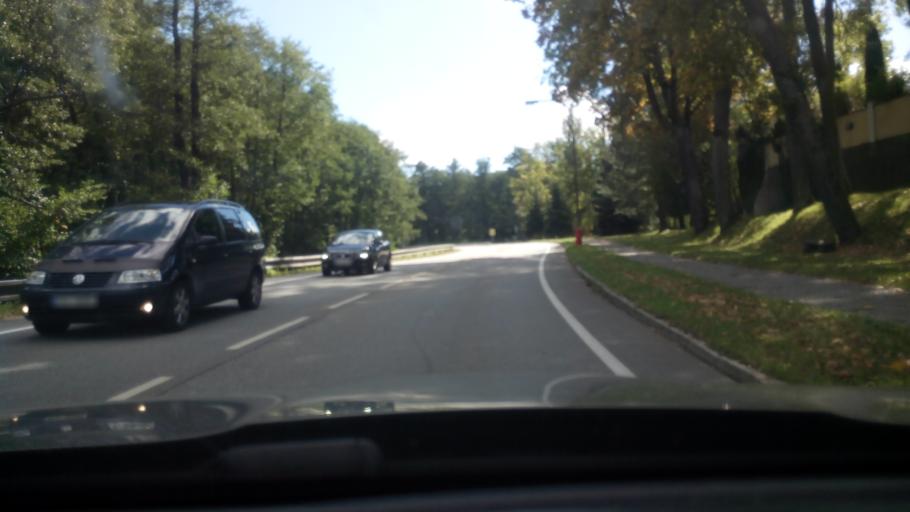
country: CZ
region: Jihocesky
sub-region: Okres Prachatice
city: Zdikov
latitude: 49.0836
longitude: 13.6980
